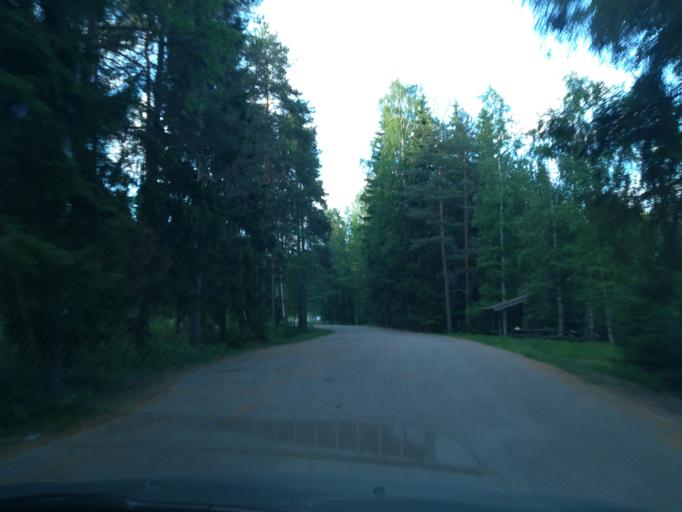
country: FI
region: Southern Savonia
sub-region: Mikkeli
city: Puumala
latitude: 61.5762
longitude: 28.1570
